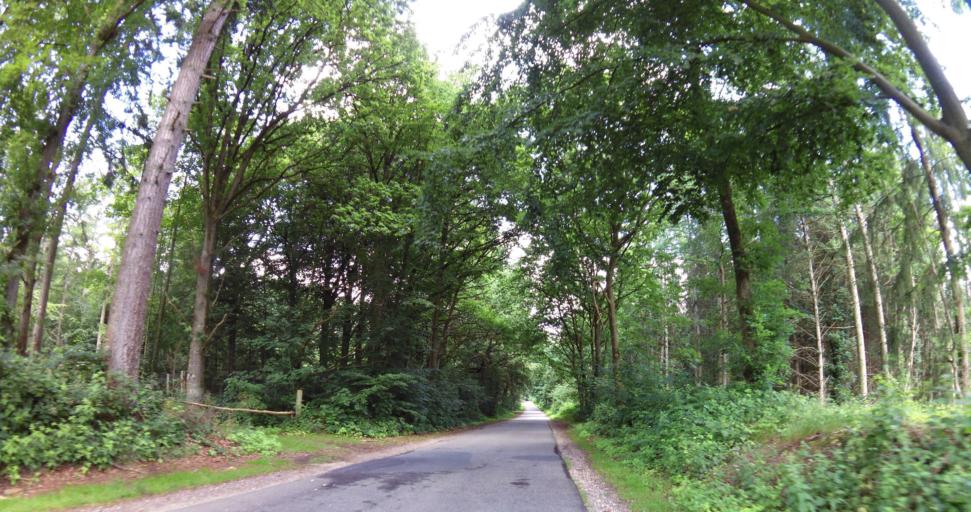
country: DE
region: Schleswig-Holstein
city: Brodersby
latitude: 54.5151
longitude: 9.7205
